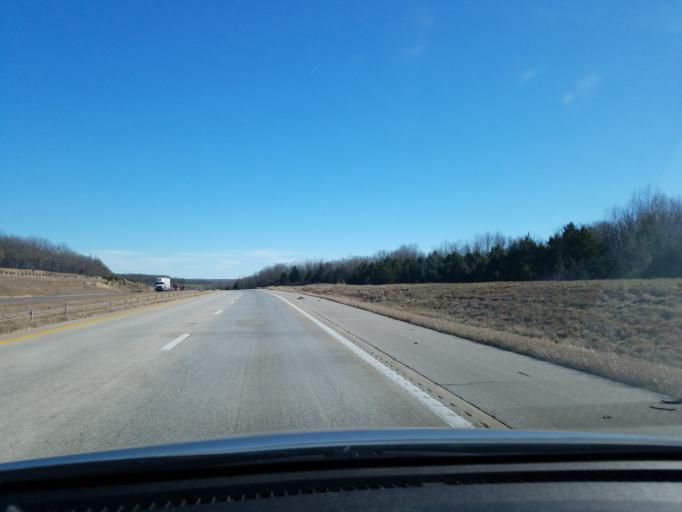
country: US
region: Missouri
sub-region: Pulaski County
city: Richland
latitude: 37.7550
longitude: -92.5037
